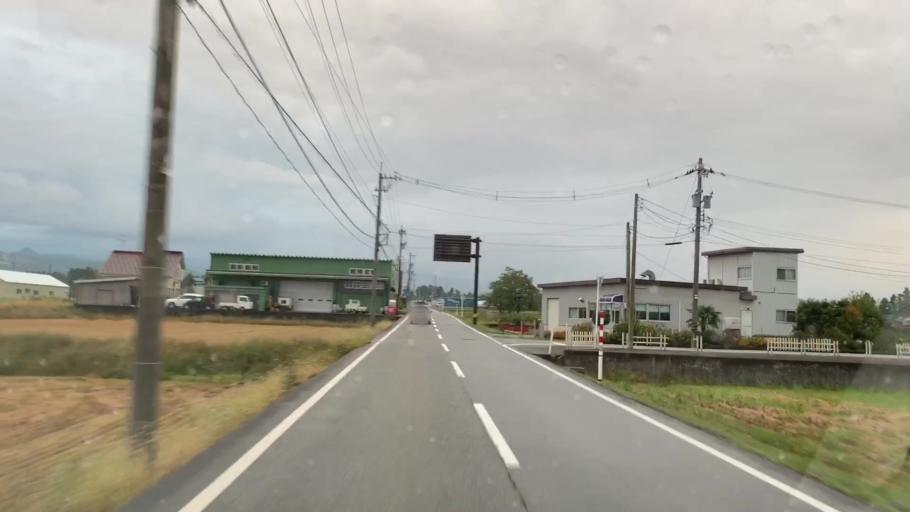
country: JP
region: Toyama
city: Kamiichi
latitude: 36.6510
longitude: 137.3287
